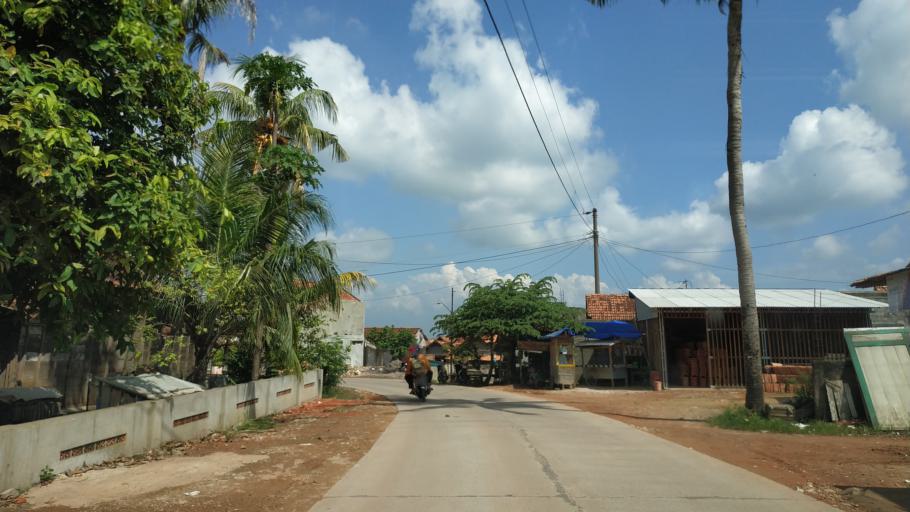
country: ID
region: Central Java
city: Jepang
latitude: -7.0101
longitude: 111.1172
